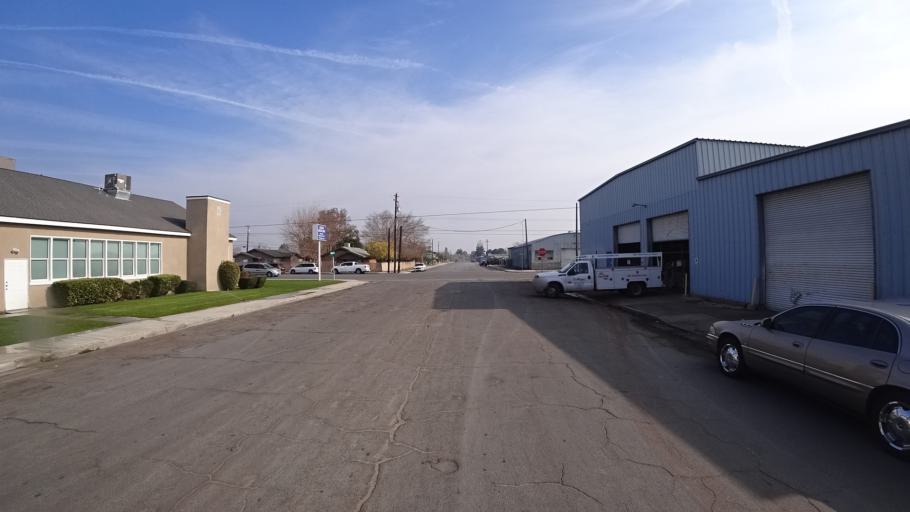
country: US
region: California
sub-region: Kern County
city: Bakersfield
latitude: 35.3697
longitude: -118.9960
